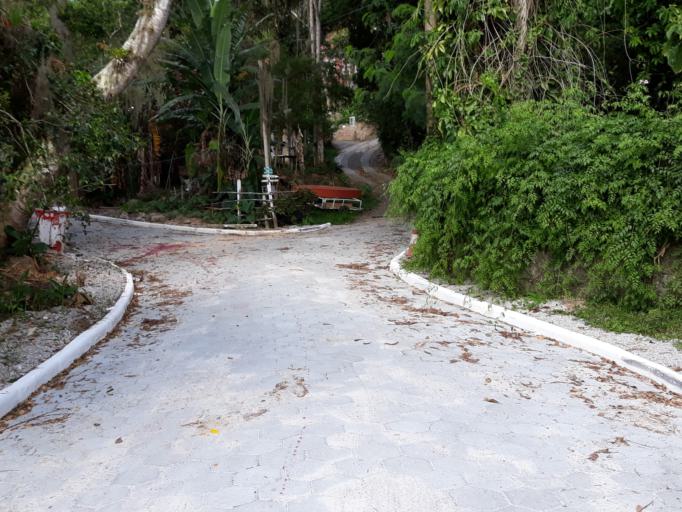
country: BR
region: Santa Catarina
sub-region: Florianopolis
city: Itacorubi
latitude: -27.4241
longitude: -48.4216
